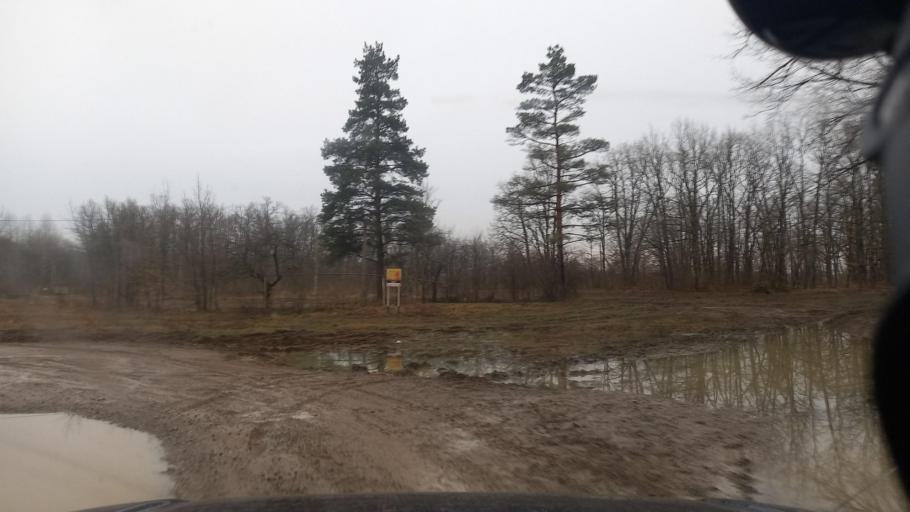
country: RU
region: Krasnodarskiy
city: Saratovskaya
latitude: 44.6612
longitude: 39.2260
